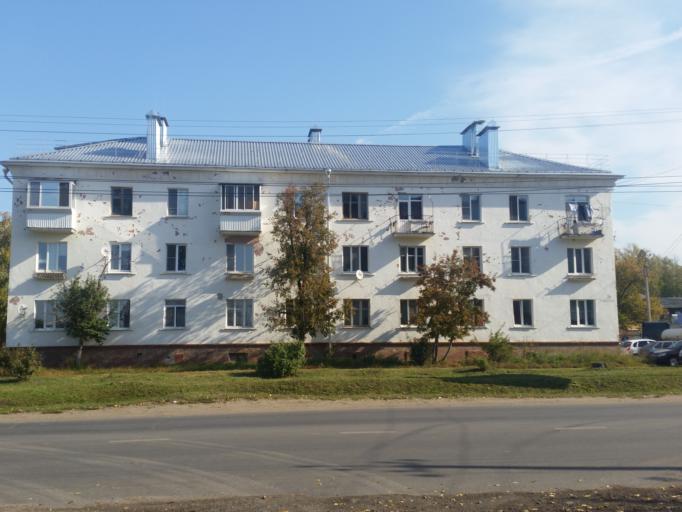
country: RU
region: Ulyanovsk
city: Dimitrovgrad
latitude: 54.2274
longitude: 49.6121
